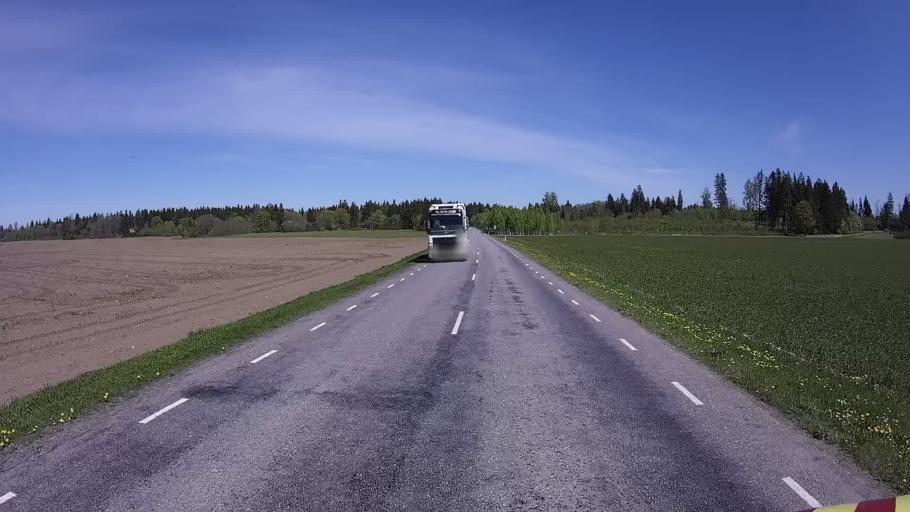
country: EE
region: Raplamaa
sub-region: Kehtna vald
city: Kehtna
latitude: 59.0535
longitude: 25.1322
